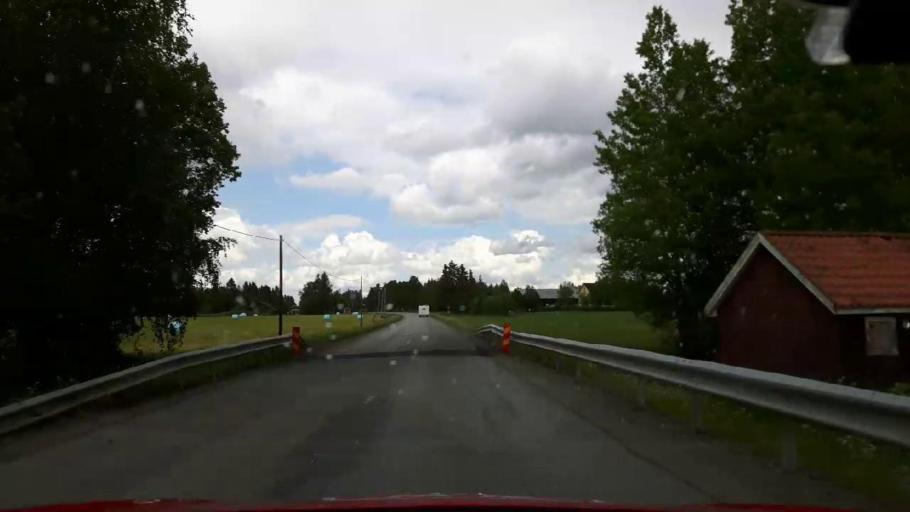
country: SE
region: Jaemtland
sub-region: Krokoms Kommun
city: Krokom
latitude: 63.5145
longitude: 14.2287
